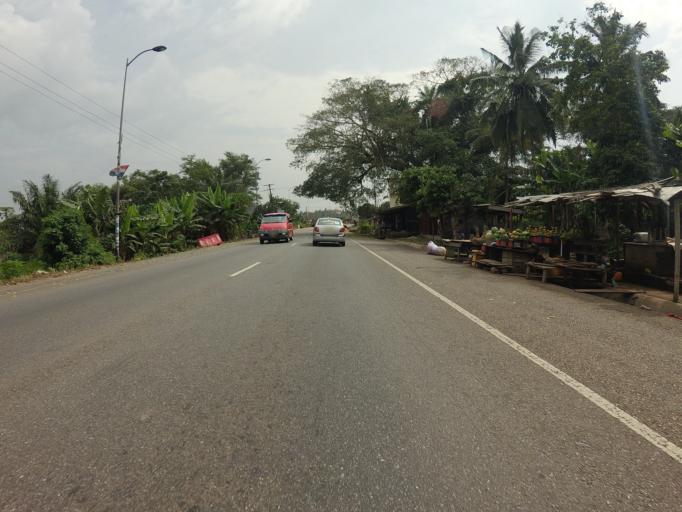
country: GH
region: Eastern
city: Aburi
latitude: 5.8215
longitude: -0.1864
